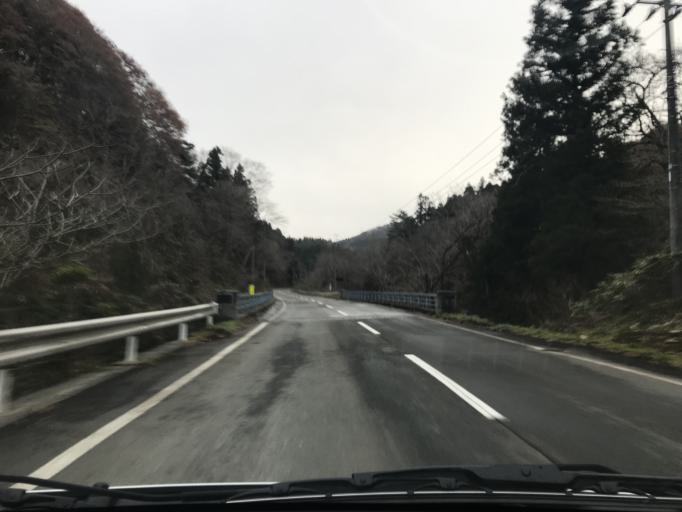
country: JP
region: Iwate
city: Tono
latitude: 39.1825
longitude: 141.3592
